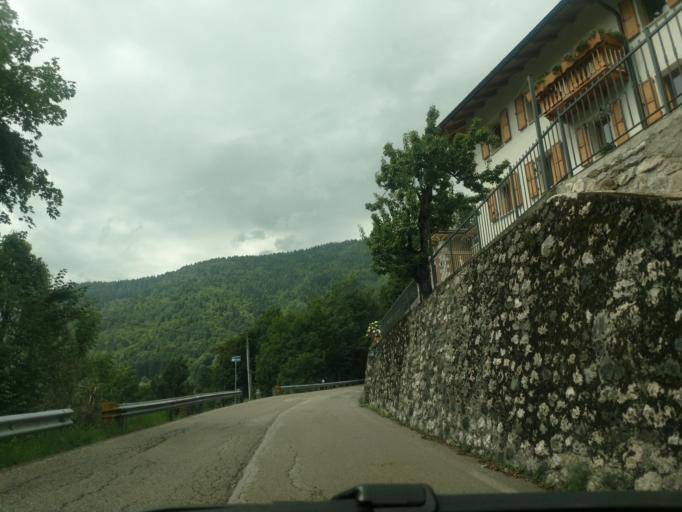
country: IT
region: Veneto
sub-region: Provincia di Belluno
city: Rivamonte Agordino
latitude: 46.2233
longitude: 11.9968
